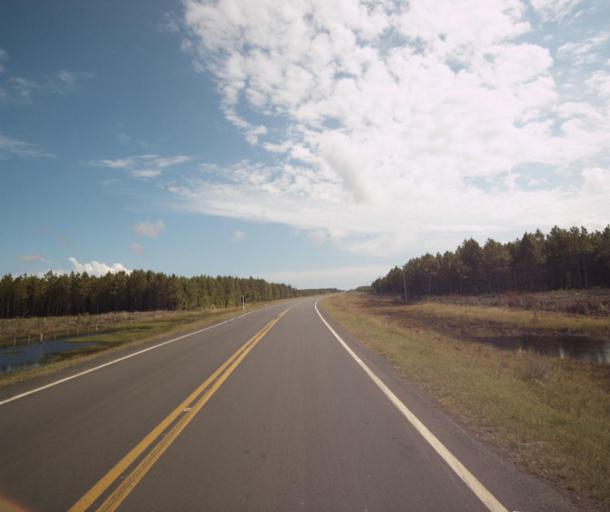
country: BR
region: Rio Grande do Sul
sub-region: Sao Lourenco Do Sul
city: Sao Lourenco do Sul
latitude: -31.5917
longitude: -51.3699
